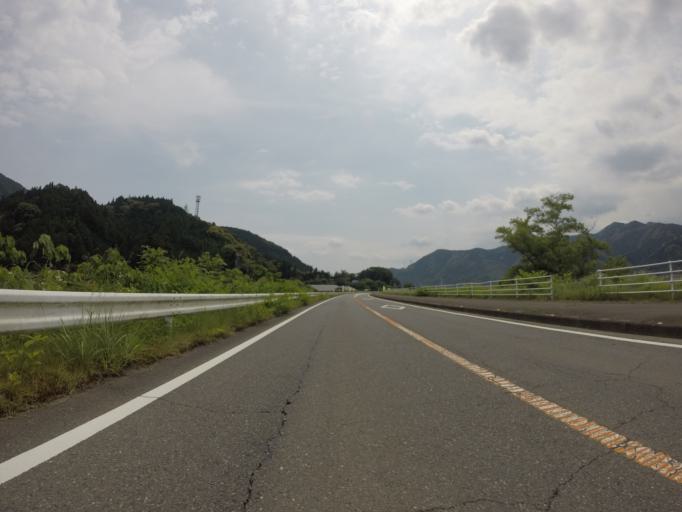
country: JP
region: Shizuoka
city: Shizuoka-shi
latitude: 35.0749
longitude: 138.3735
